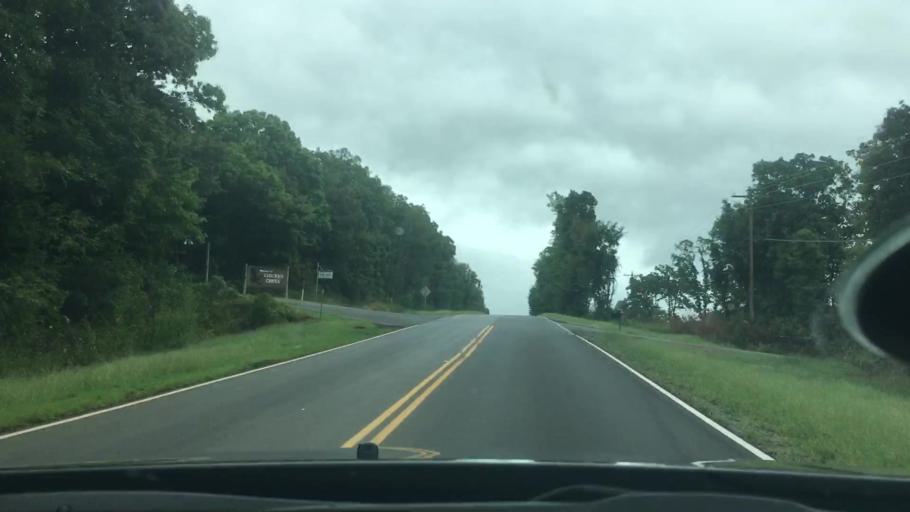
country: US
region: Oklahoma
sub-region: Sequoyah County
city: Vian
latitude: 35.6688
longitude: -94.9353
